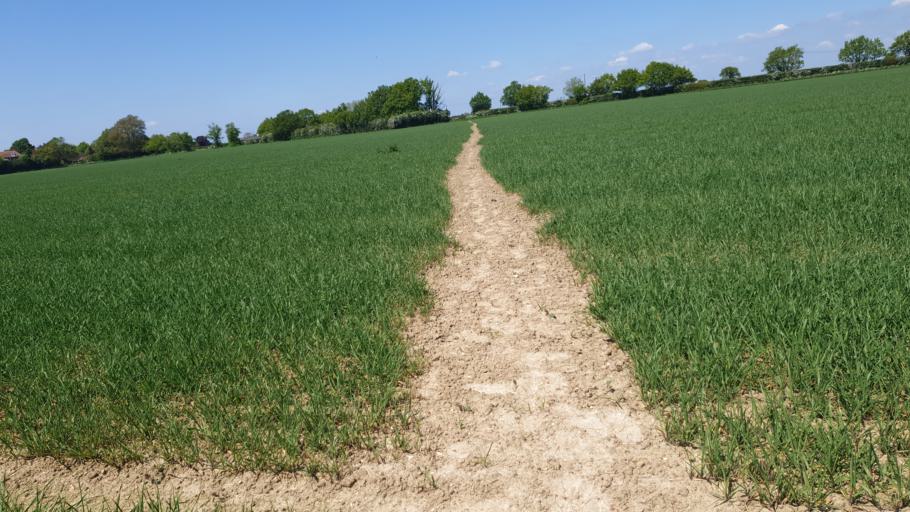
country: GB
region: England
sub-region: Essex
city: Manningtree
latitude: 51.9095
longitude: 1.0501
